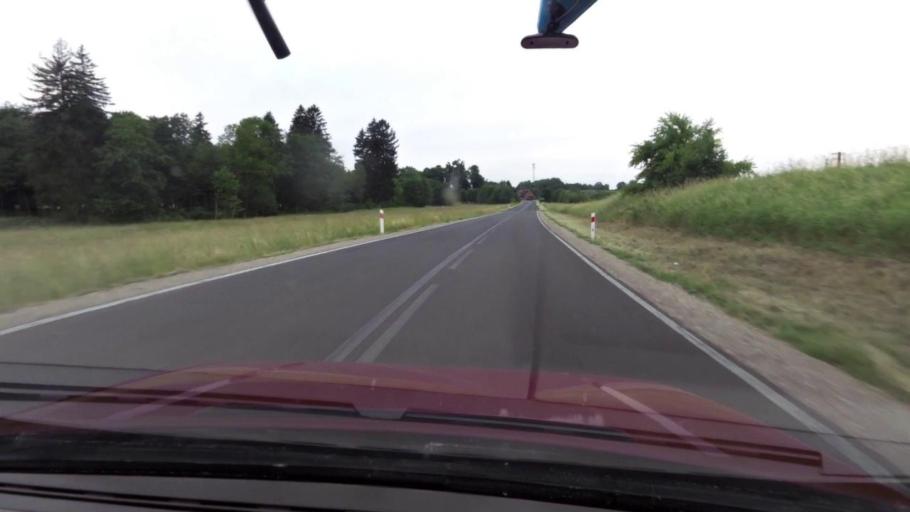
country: PL
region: West Pomeranian Voivodeship
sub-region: Powiat koszalinski
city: Sianow
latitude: 54.1589
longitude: 16.4523
